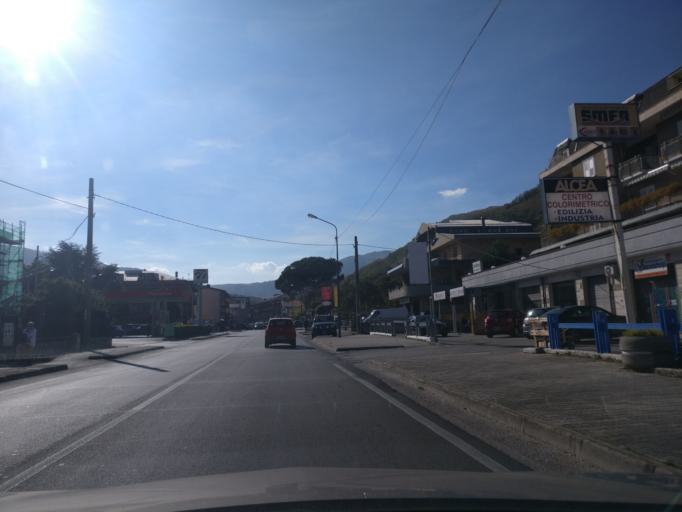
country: IT
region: Campania
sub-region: Provincia di Avellino
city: Monteforte Irpino
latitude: 40.9057
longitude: 14.7459
